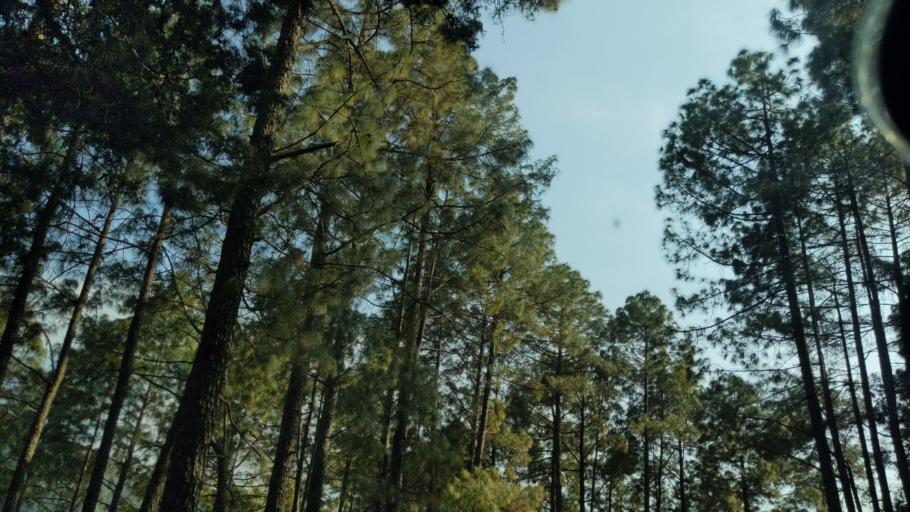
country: IN
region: Uttarakhand
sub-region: Naini Tal
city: Bhowali
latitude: 29.3998
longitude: 79.5383
